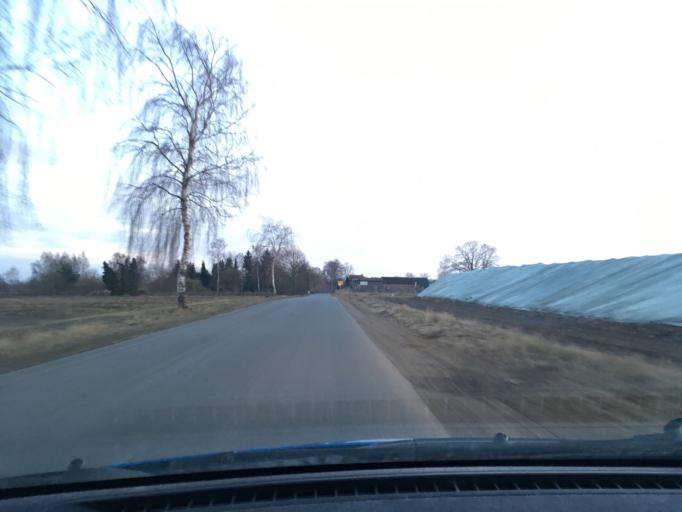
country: DE
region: Lower Saxony
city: Dahlenburg
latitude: 53.1844
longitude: 10.6965
